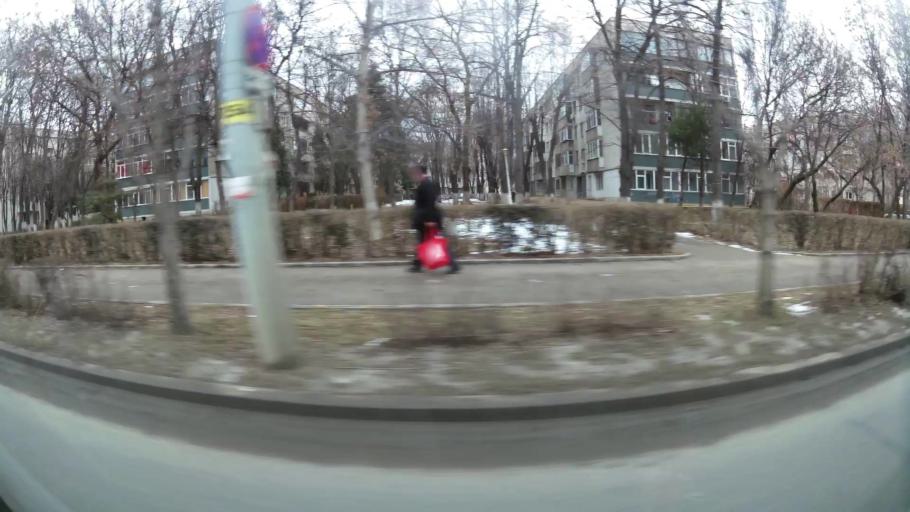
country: RO
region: Prahova
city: Ploiesti
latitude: 44.9294
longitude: 26.0324
